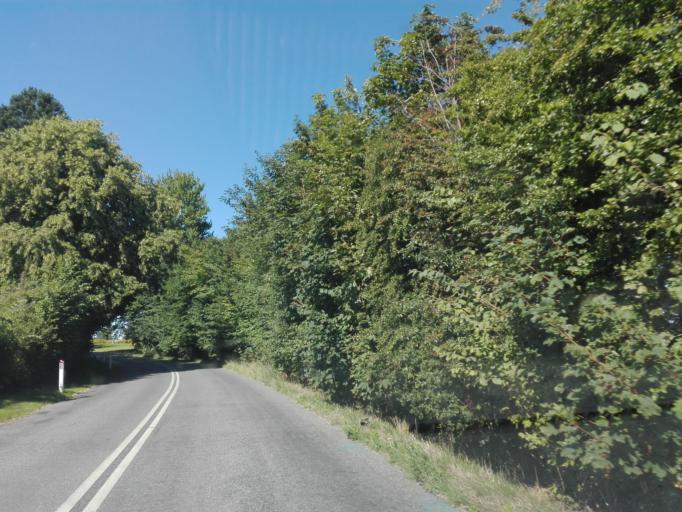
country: DK
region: Central Jutland
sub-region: Arhus Kommune
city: Beder
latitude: 56.0277
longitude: 10.2600
